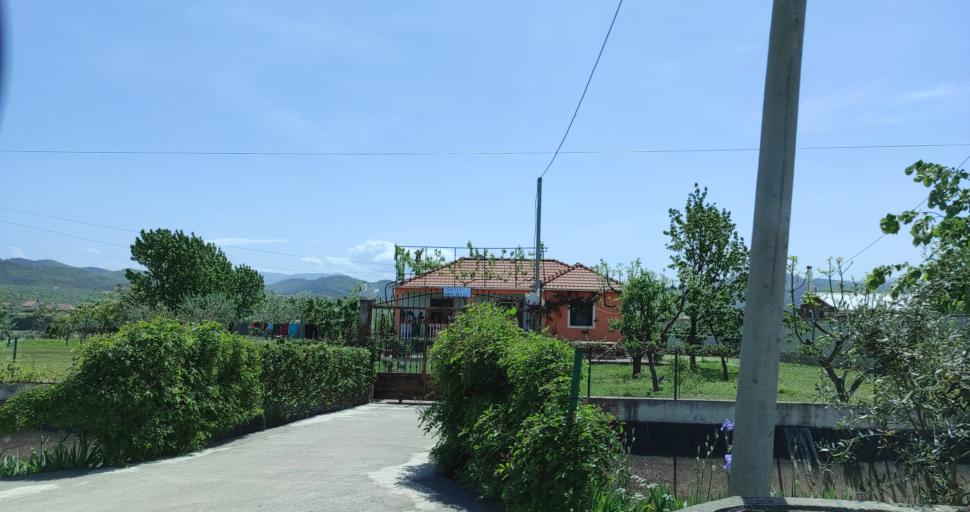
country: AL
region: Shkoder
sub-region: Rrethi i Shkodres
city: Shkoder
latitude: 42.1075
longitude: 19.5620
